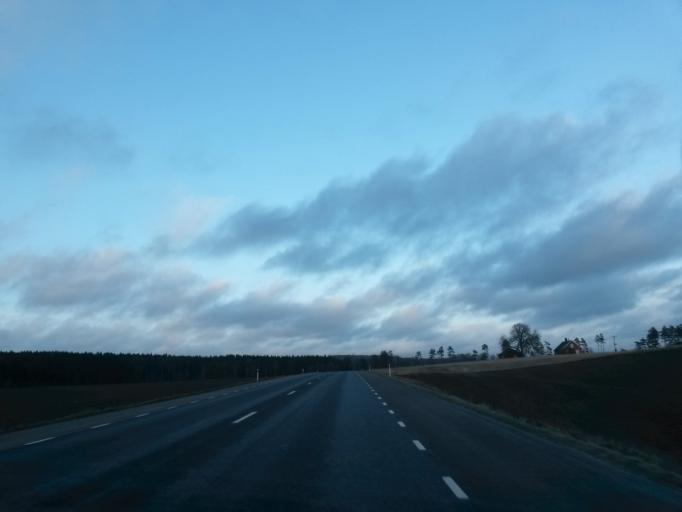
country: SE
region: Halland
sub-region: Halmstads Kommun
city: Aled
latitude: 56.7306
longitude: 12.9114
